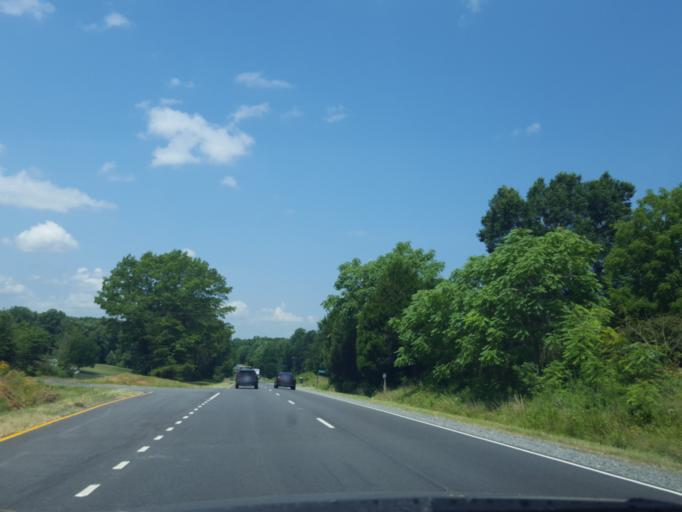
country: US
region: Virginia
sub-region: Spotsylvania County
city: Spotsylvania
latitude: 38.3211
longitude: -77.6998
